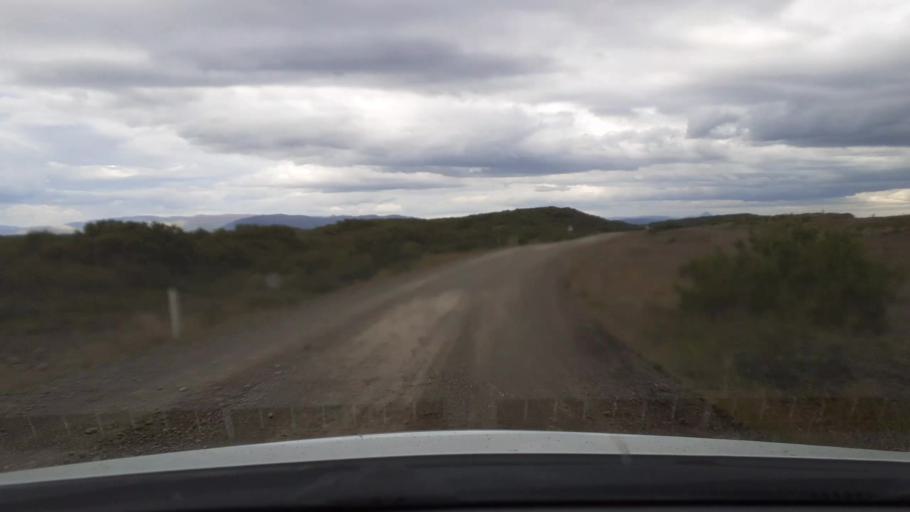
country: IS
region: West
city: Borgarnes
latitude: 64.5937
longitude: -21.9867
